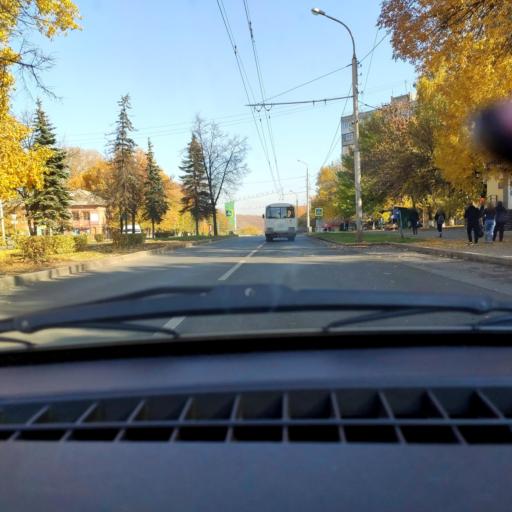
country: RU
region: Bashkortostan
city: Ufa
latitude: 54.8114
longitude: 56.1210
